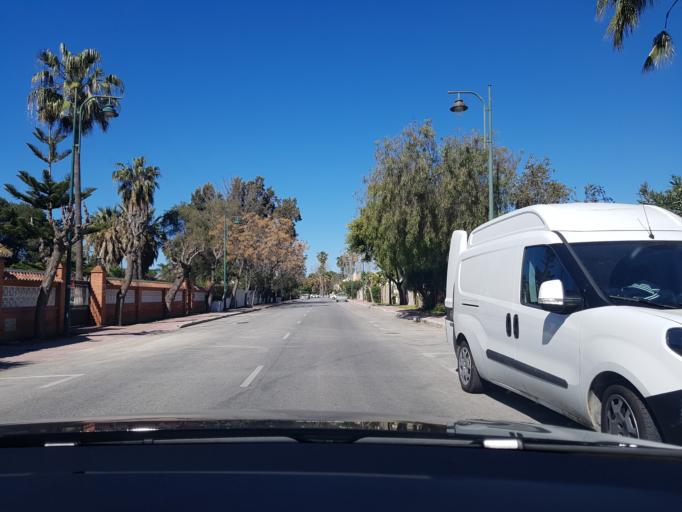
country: ES
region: Andalusia
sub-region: Provincia de Malaga
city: Torremolinos
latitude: 36.6670
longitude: -4.4589
